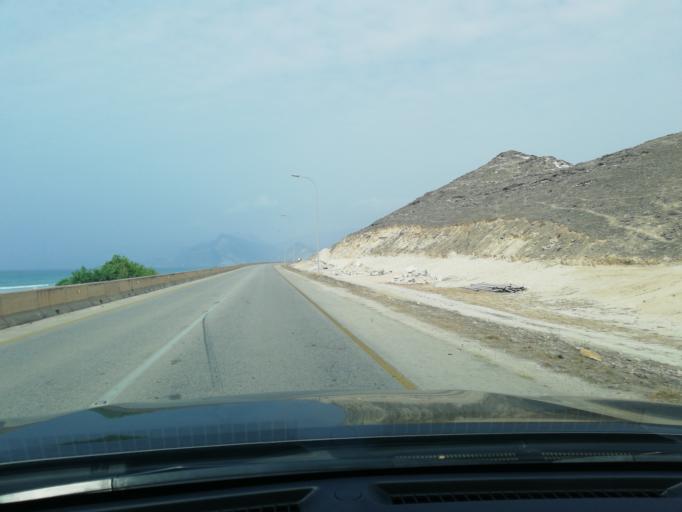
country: OM
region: Zufar
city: Salalah
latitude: 16.8859
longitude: 53.8108
